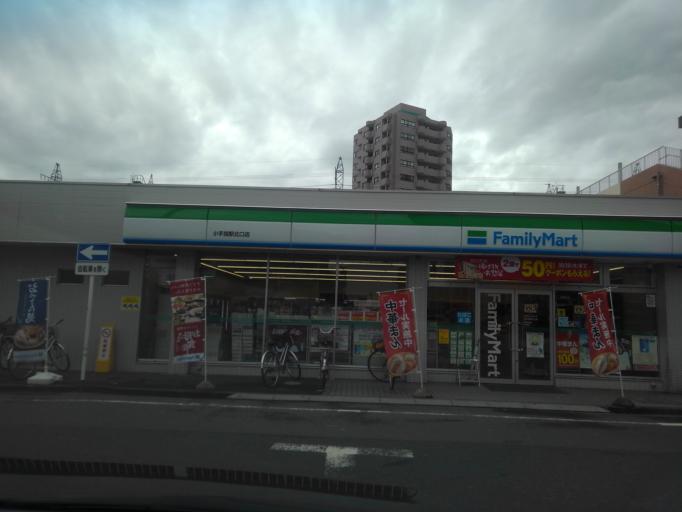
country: JP
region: Saitama
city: Tokorozawa
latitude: 35.8011
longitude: 139.4385
